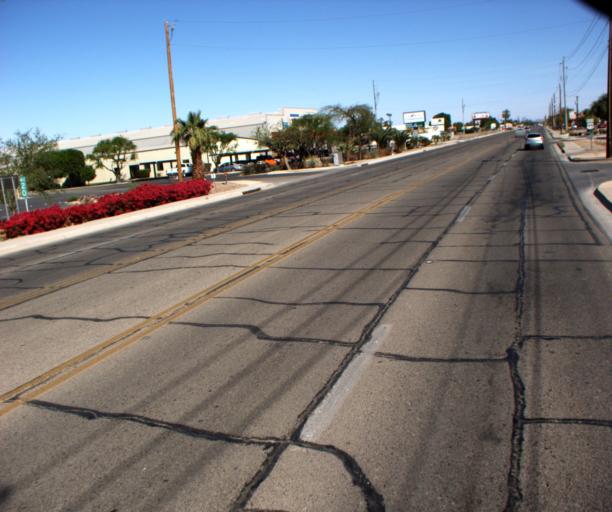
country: US
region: Arizona
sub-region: Yuma County
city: Yuma
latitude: 32.6708
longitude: -114.6501
